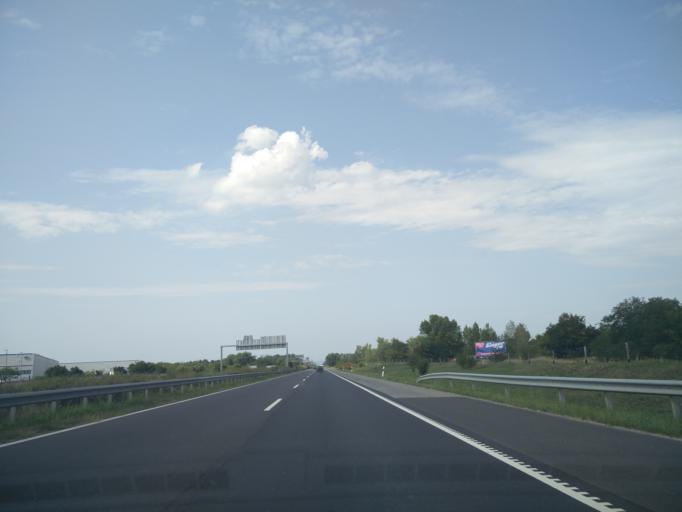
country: HU
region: Pest
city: Gyal
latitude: 47.3644
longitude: 19.1931
